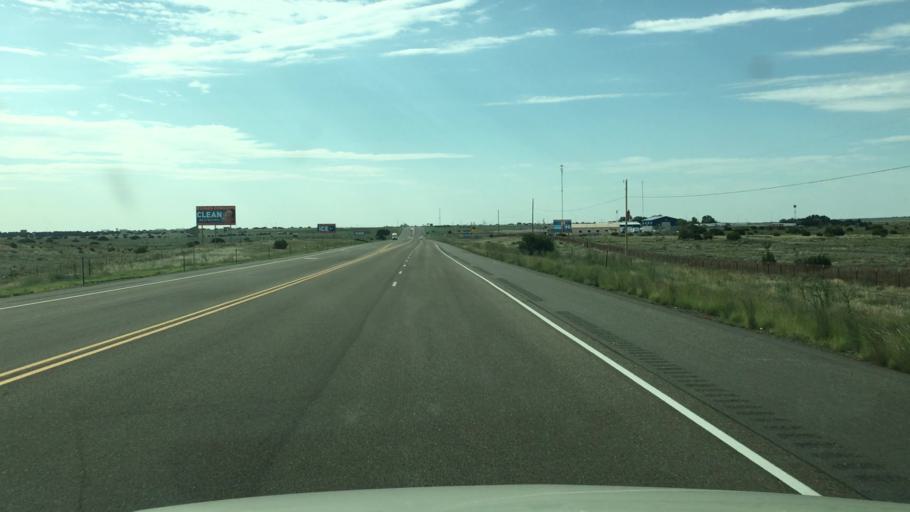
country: US
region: New Mexico
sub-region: Torrance County
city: Moriarty
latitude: 35.0201
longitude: -105.6709
